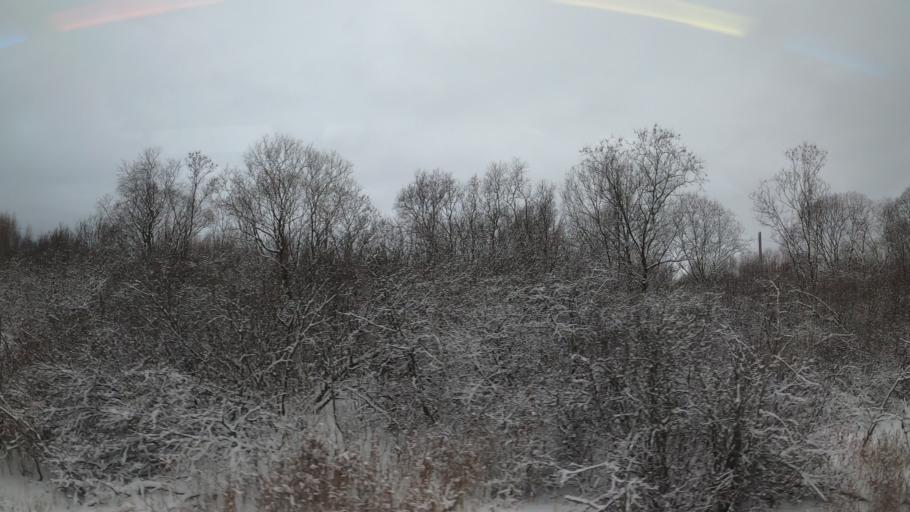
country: RU
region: Jaroslavl
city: Pereslavl'-Zalesskiy
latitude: 56.7273
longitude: 38.9033
